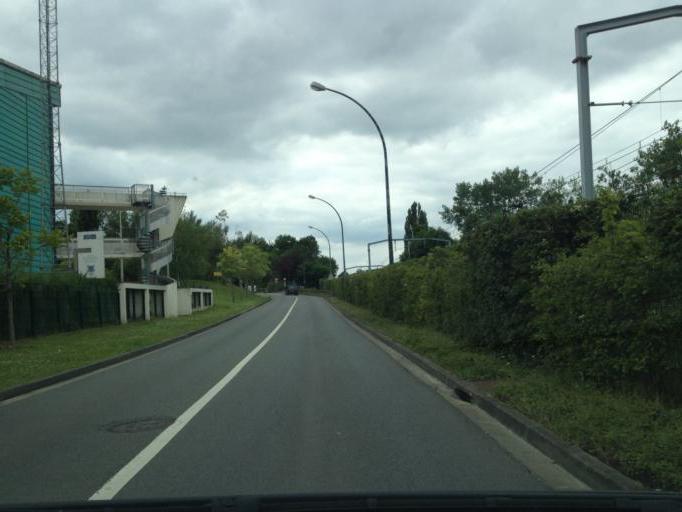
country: FR
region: Ile-de-France
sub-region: Departement de l'Essonne
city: Gif-sur-Yvette
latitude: 48.6980
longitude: 2.1269
